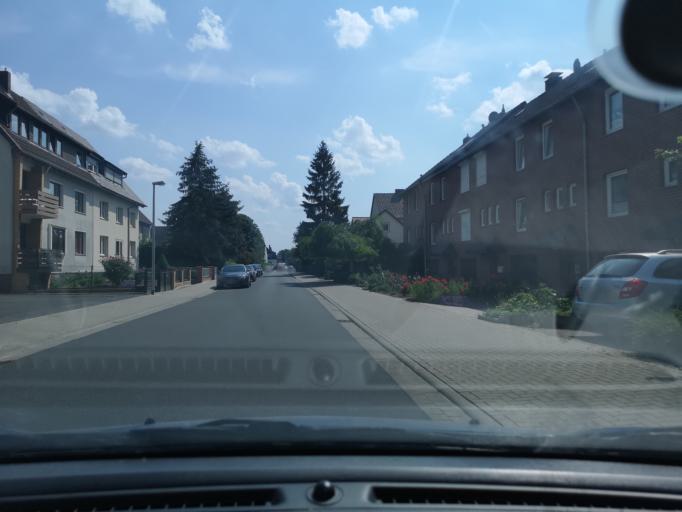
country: DE
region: Lower Saxony
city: Langenhagen
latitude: 52.4357
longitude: 9.7383
